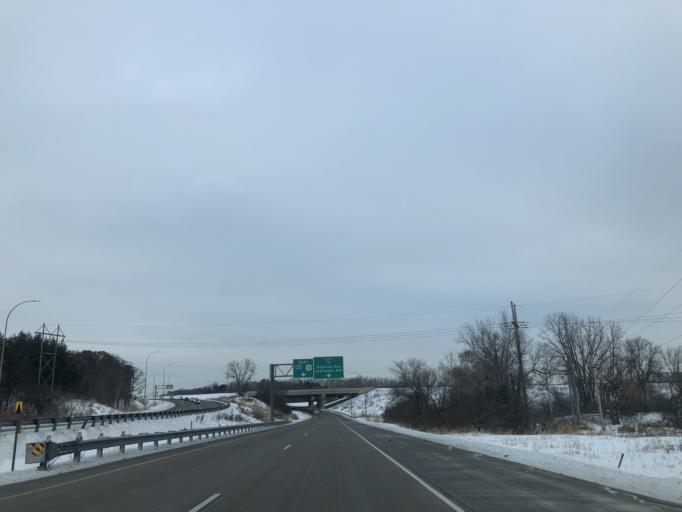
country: US
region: Minnesota
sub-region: Ramsey County
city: Arden Hills
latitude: 45.0693
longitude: -93.1678
